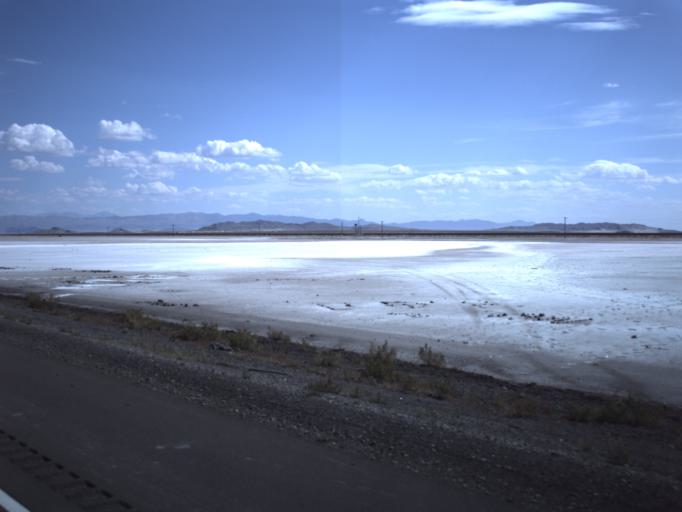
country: US
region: Utah
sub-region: Tooele County
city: Wendover
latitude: 40.7284
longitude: -113.3957
